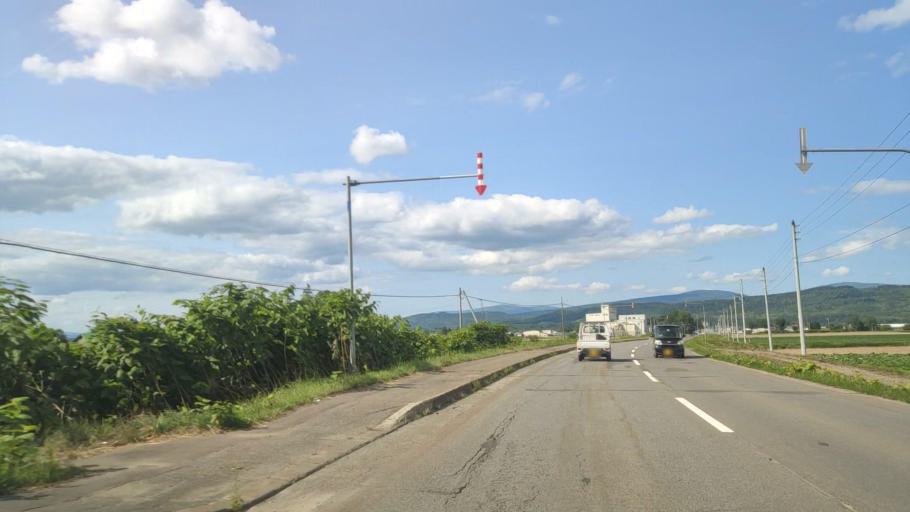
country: JP
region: Hokkaido
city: Nayoro
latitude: 44.4283
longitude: 142.3998
